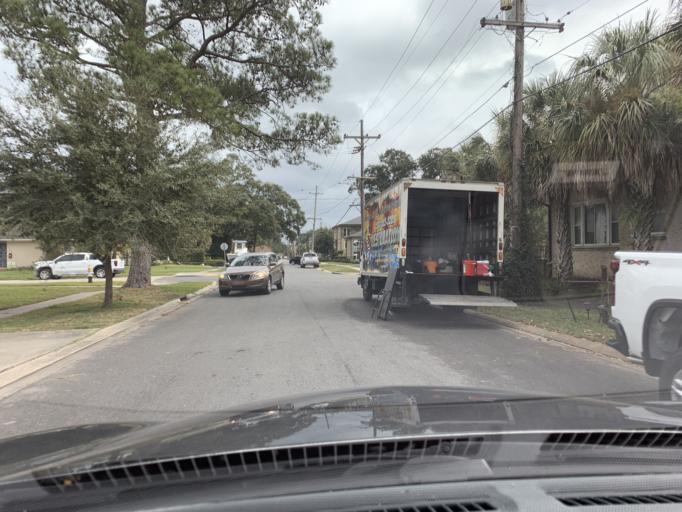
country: US
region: Louisiana
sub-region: Jefferson Parish
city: Metairie
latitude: 30.0174
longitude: -90.1037
